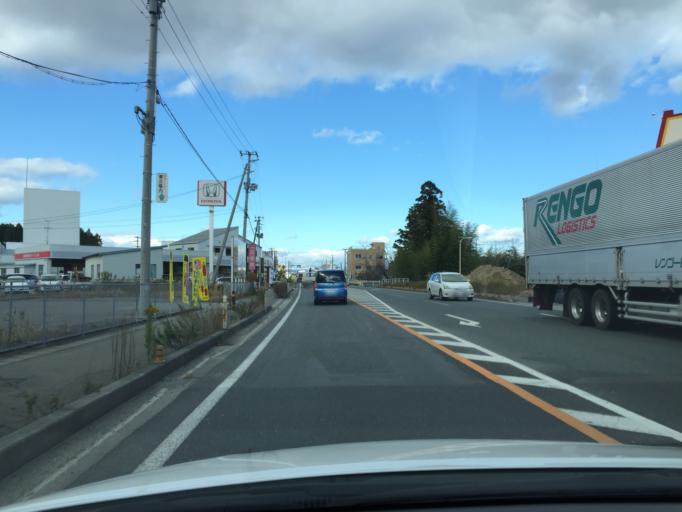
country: JP
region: Fukushima
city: Namie
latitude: 37.6288
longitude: 140.9892
